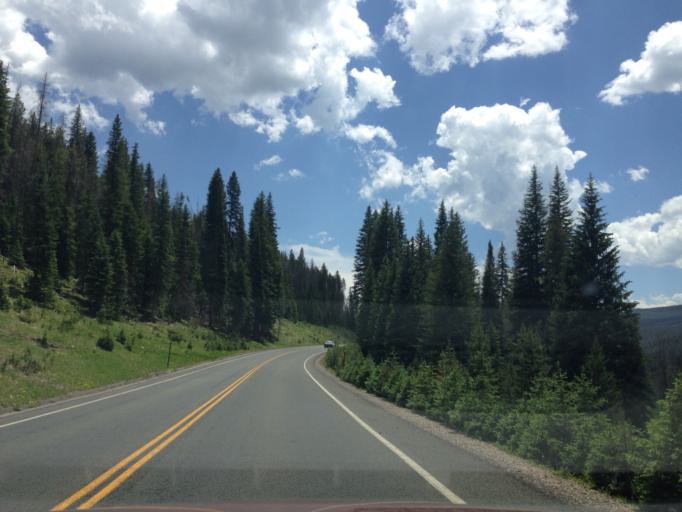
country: US
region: Colorado
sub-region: Grand County
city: Granby
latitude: 40.3488
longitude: -105.8574
